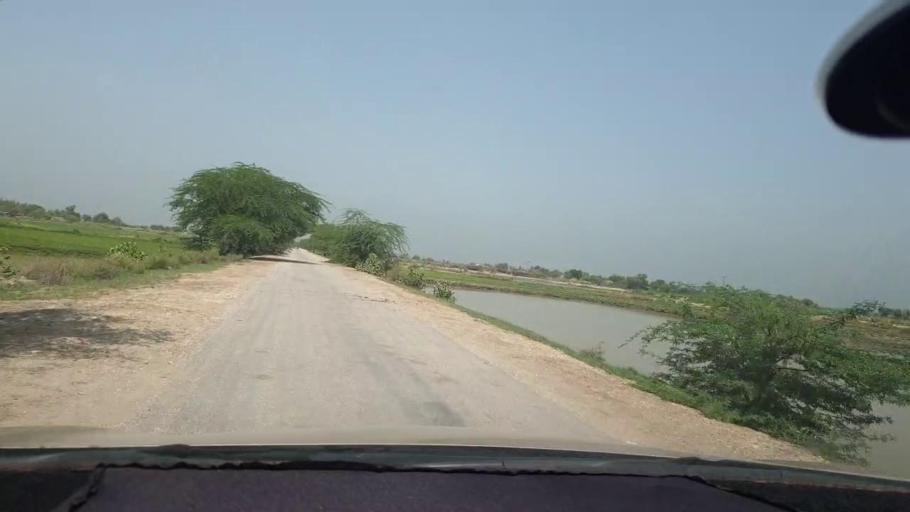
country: PK
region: Sindh
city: Kambar
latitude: 27.6694
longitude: 67.9131
